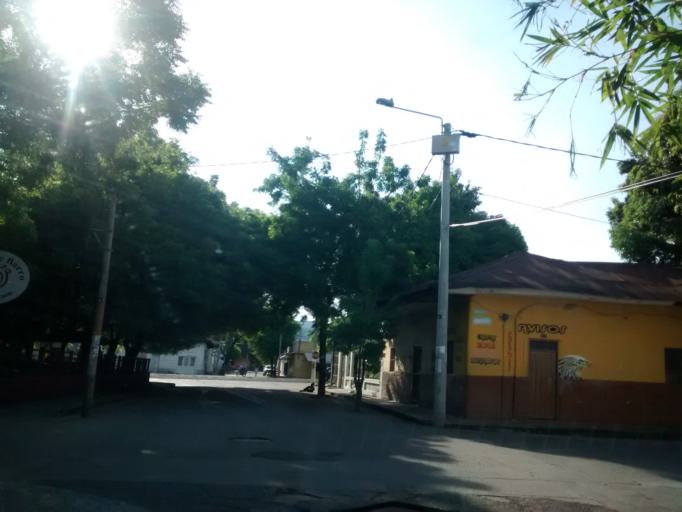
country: CO
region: Cundinamarca
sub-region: Girardot
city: Girardot City
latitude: 4.2997
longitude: -74.8067
